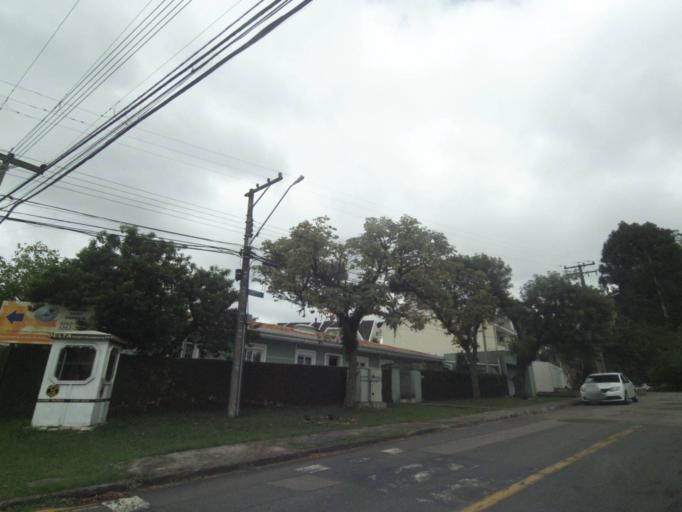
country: BR
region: Parana
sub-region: Pinhais
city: Pinhais
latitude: -25.4088
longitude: -49.2243
